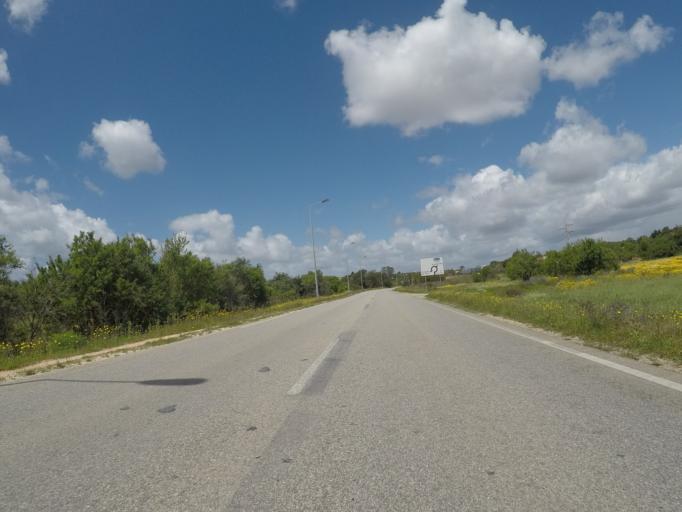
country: PT
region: Faro
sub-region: Silves
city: Armacao de Pera
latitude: 37.1165
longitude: -8.3477
